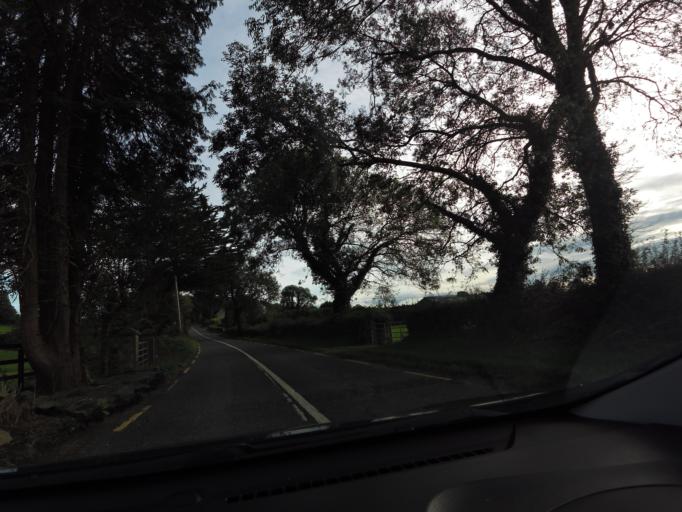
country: IE
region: Connaught
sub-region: County Galway
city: Ballinasloe
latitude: 53.3230
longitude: -8.2796
